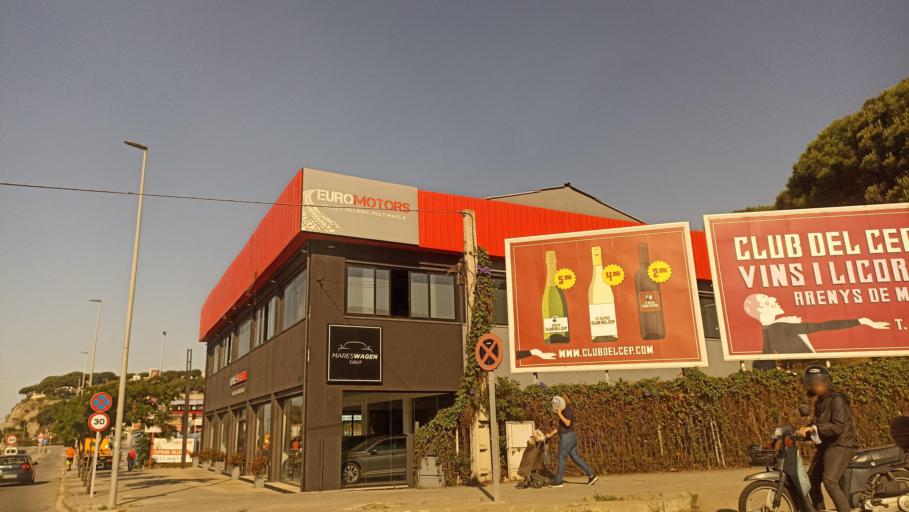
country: ES
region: Catalonia
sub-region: Provincia de Barcelona
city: Arenys de Mar
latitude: 41.5759
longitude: 2.5440
